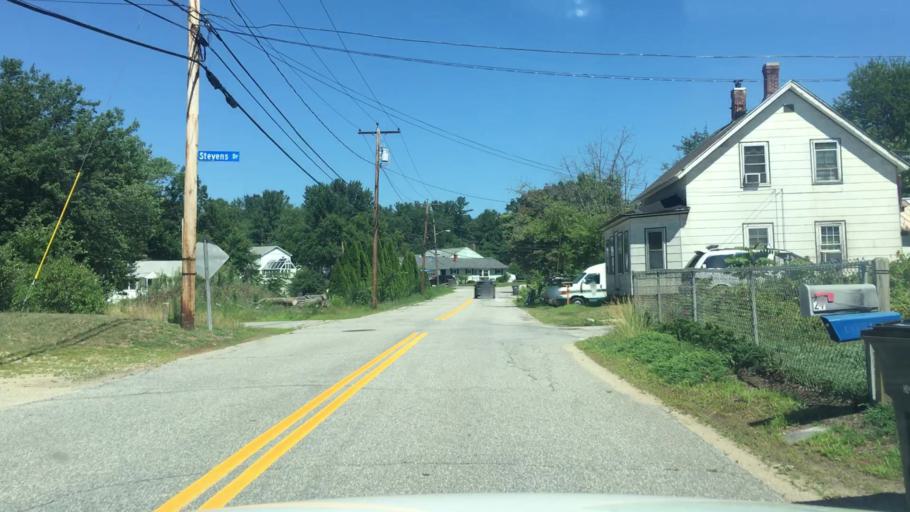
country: US
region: New Hampshire
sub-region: Merrimack County
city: Hooksett
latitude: 43.0992
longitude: -71.4591
